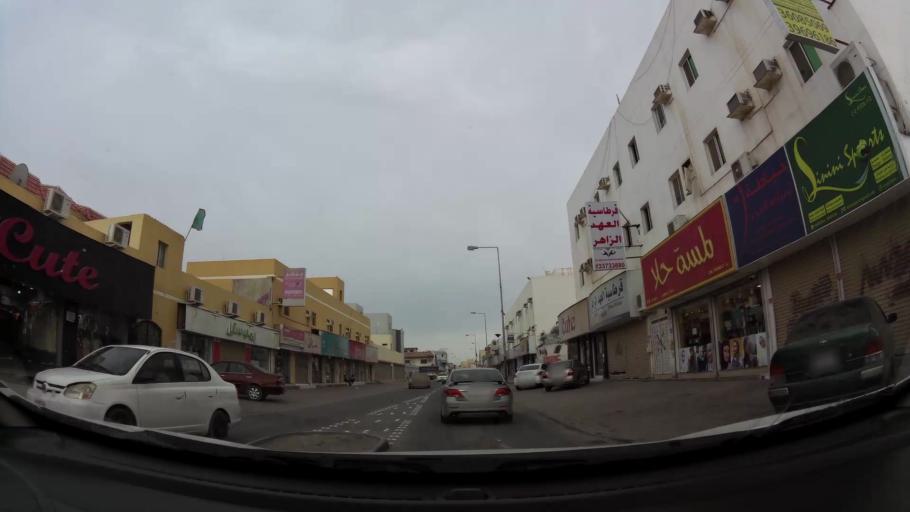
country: BH
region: Central Governorate
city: Madinat Hamad
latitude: 26.0955
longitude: 50.4867
